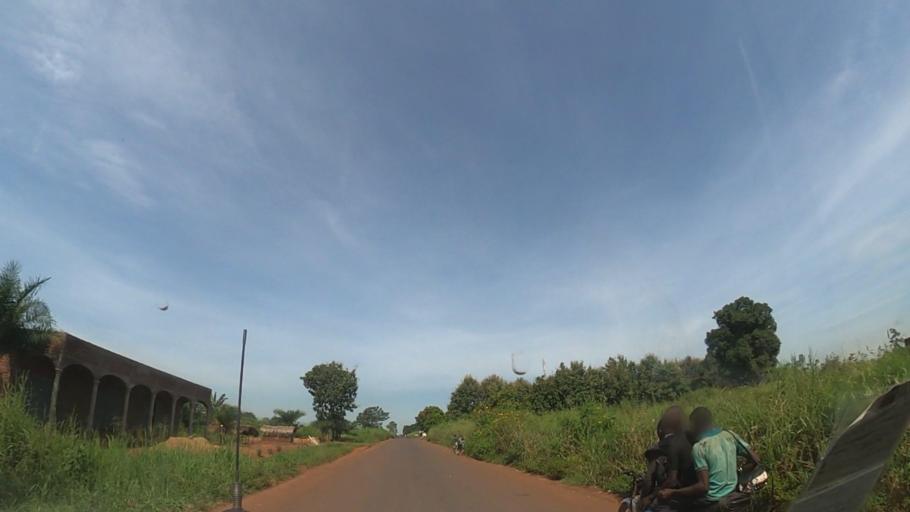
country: CF
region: Ombella-Mpoko
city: Bimbo
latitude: 4.3130
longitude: 18.4743
